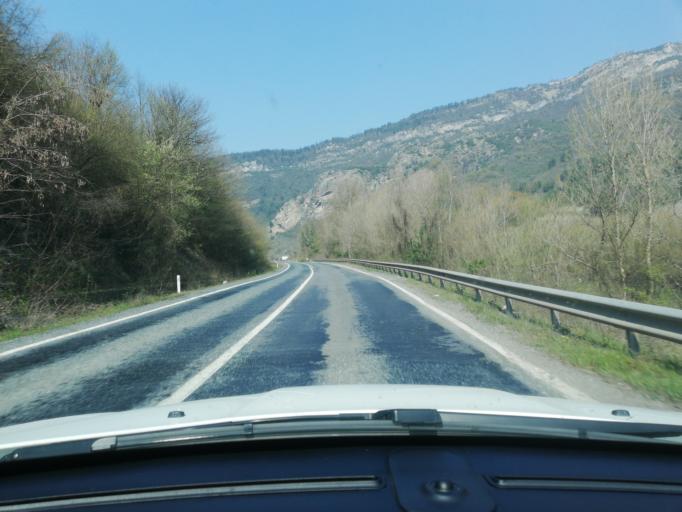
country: TR
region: Karabuk
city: Yenice
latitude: 41.2178
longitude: 32.2452
